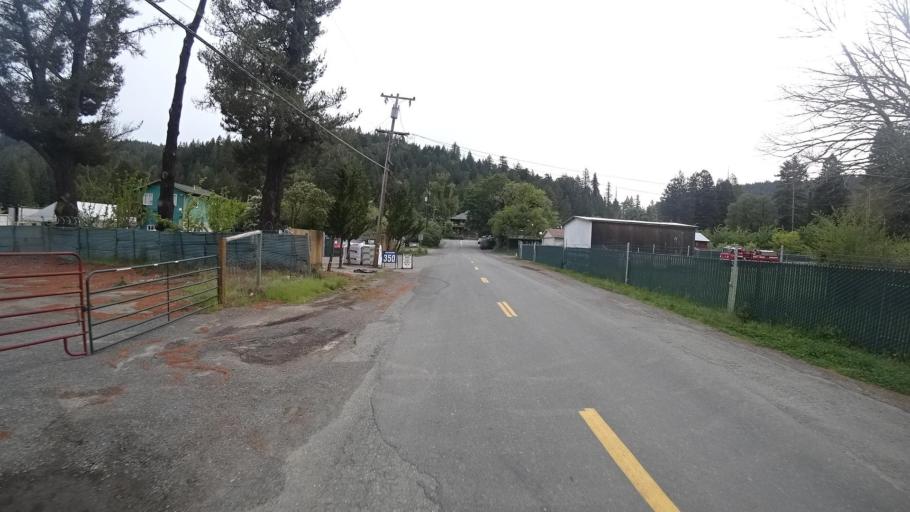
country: US
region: California
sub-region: Humboldt County
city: Redway
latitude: 40.2659
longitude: -123.8737
